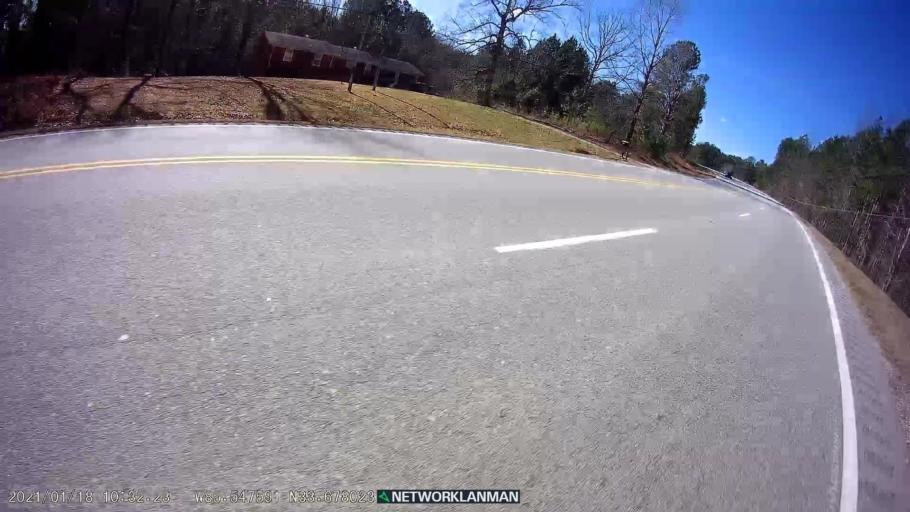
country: US
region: Alabama
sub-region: Cleburne County
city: Heflin
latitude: 33.6780
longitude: -85.5479
